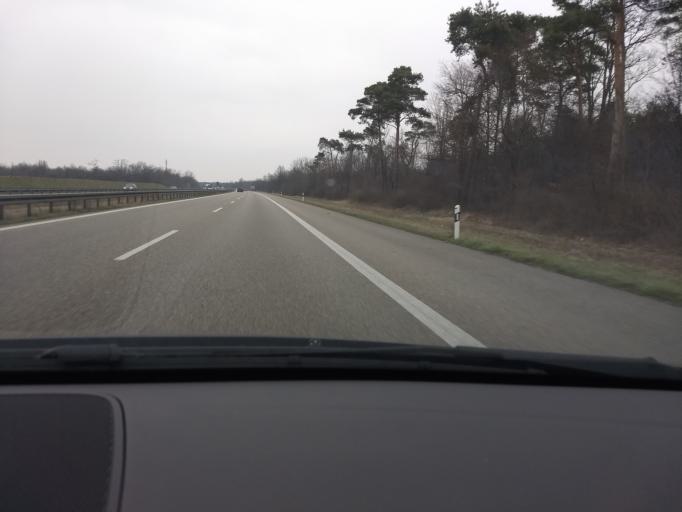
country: DE
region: Baden-Wuerttemberg
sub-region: Freiburg Region
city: Neuenburg am Rhein
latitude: 47.8378
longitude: 7.5661
